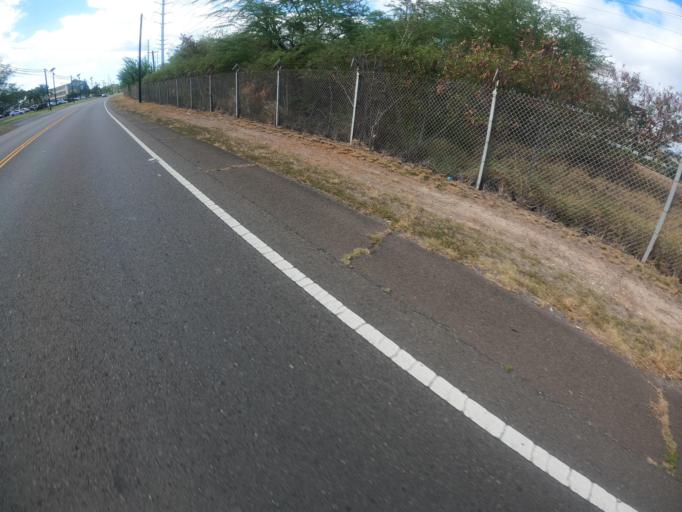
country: US
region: Hawaii
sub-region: Honolulu County
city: Makakilo City
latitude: 21.3228
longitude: -158.0755
